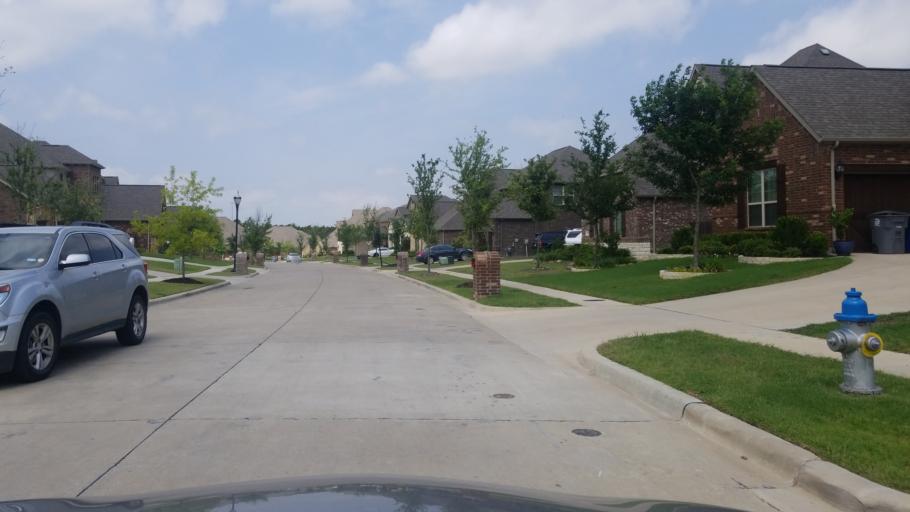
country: US
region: Texas
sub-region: Dallas County
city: Duncanville
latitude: 32.6819
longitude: -96.9363
